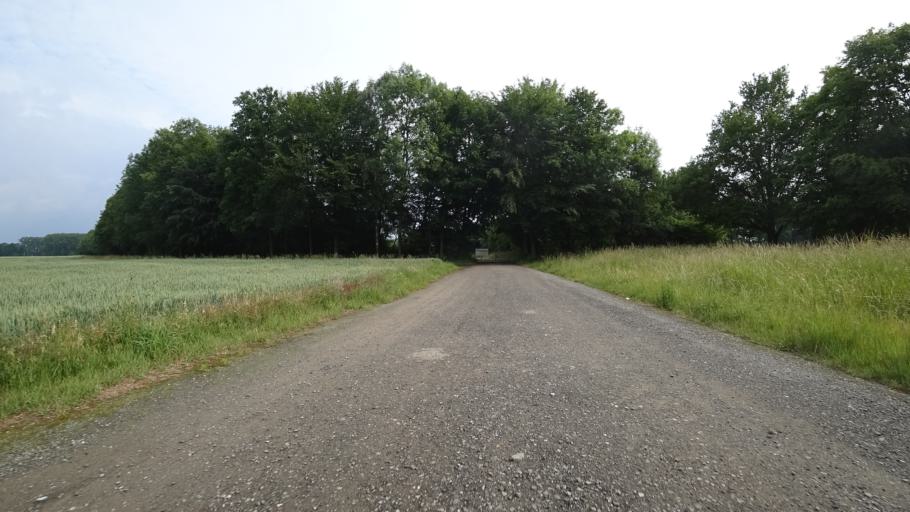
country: DE
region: North Rhine-Westphalia
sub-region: Regierungsbezirk Detmold
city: Guetersloh
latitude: 51.9428
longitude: 8.3529
